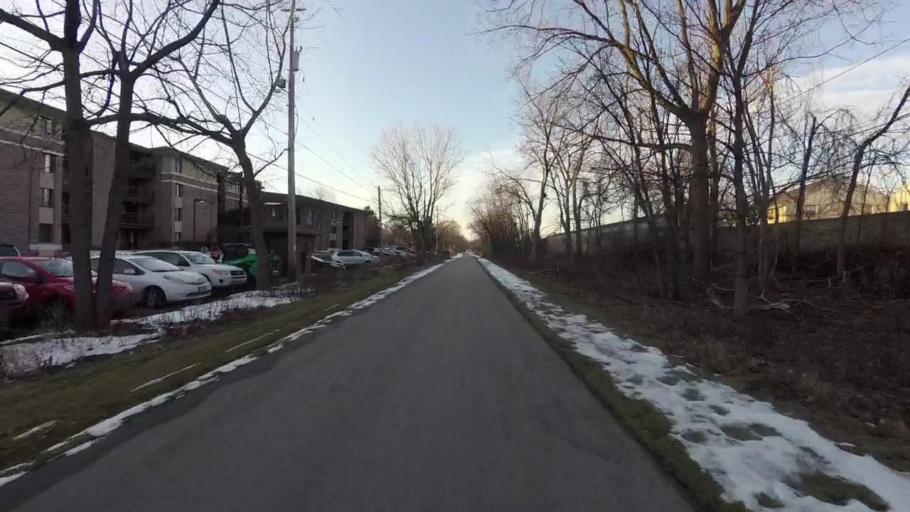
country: US
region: Wisconsin
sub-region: Milwaukee County
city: Whitefish Bay
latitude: 43.1046
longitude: -87.9101
